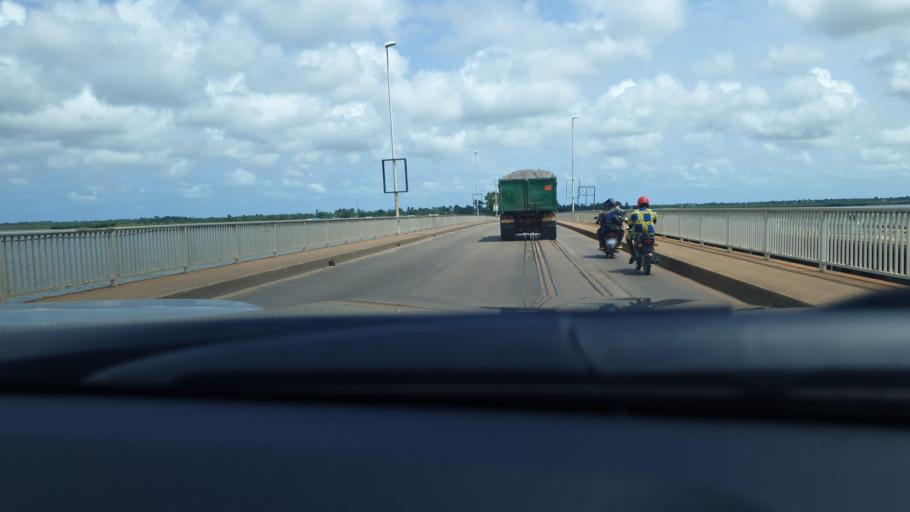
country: BJ
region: Queme
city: Porto-Novo
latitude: 6.4664
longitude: 2.6198
